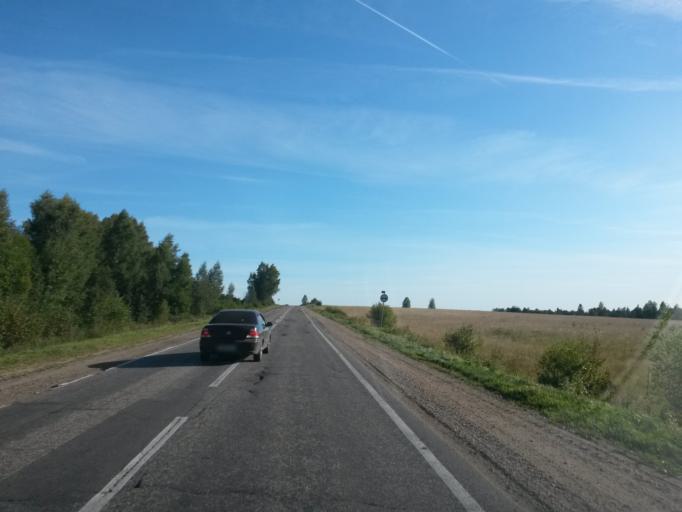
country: RU
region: Jaroslavl
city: Krasnyye Tkachi
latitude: 57.4654
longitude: 39.9086
